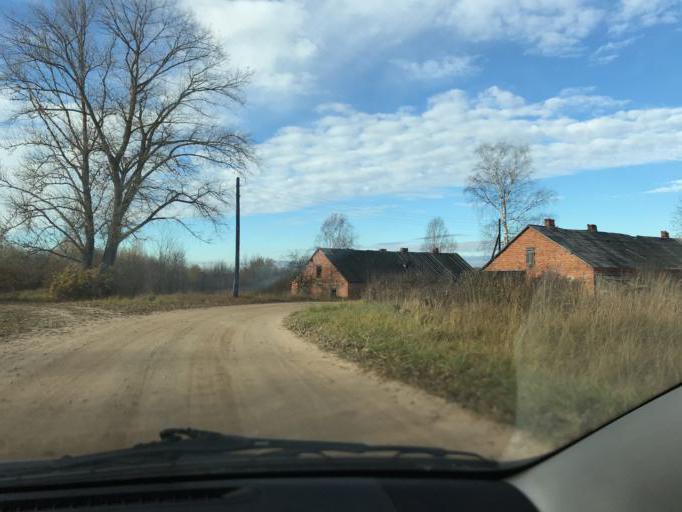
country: BY
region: Vitebsk
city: Haradok
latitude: 55.4529
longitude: 30.0377
